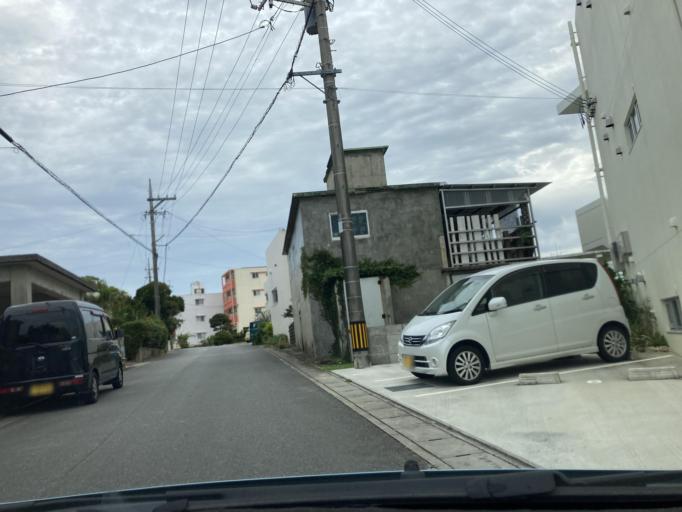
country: JP
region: Okinawa
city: Ishikawa
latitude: 26.4038
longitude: 127.7388
